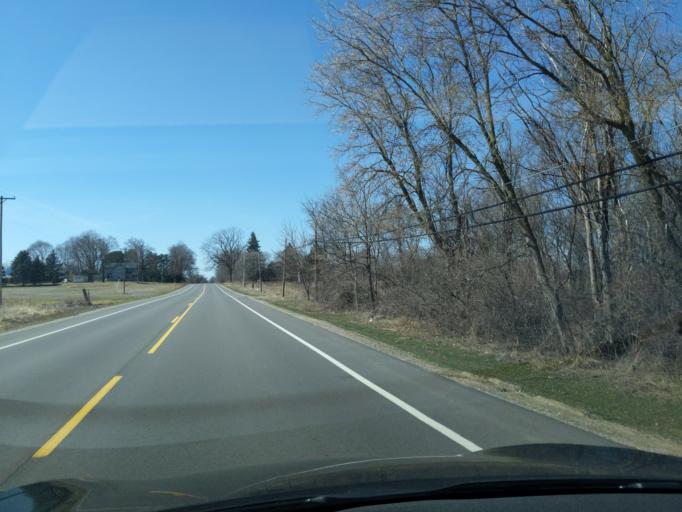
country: US
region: Michigan
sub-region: Eaton County
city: Grand Ledge
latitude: 42.7264
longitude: -84.7291
